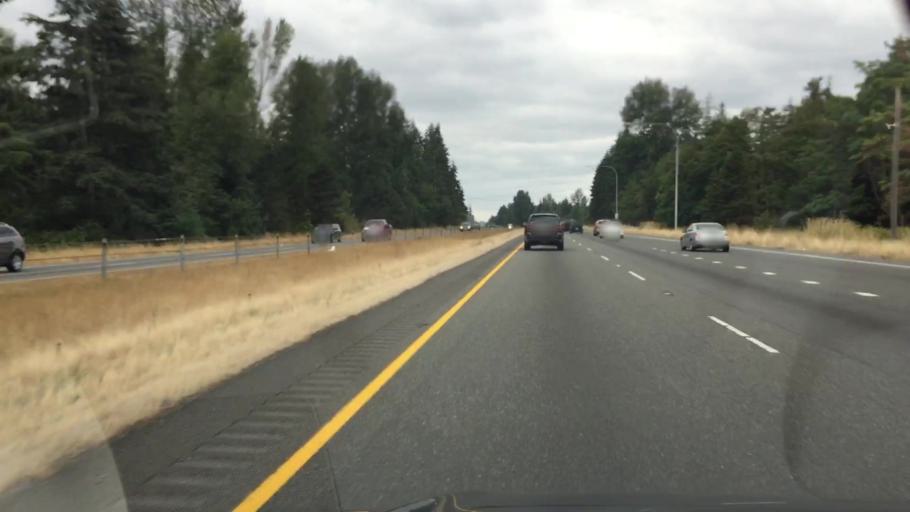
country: US
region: Washington
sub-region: Pierce County
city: Summit
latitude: 47.1585
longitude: -122.3638
